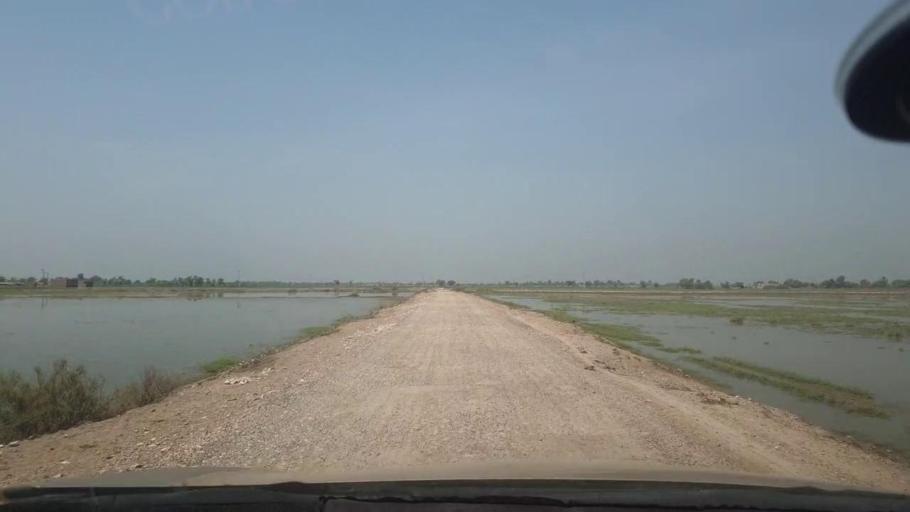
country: PK
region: Sindh
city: Shahdadkot
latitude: 27.7539
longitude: 67.9318
